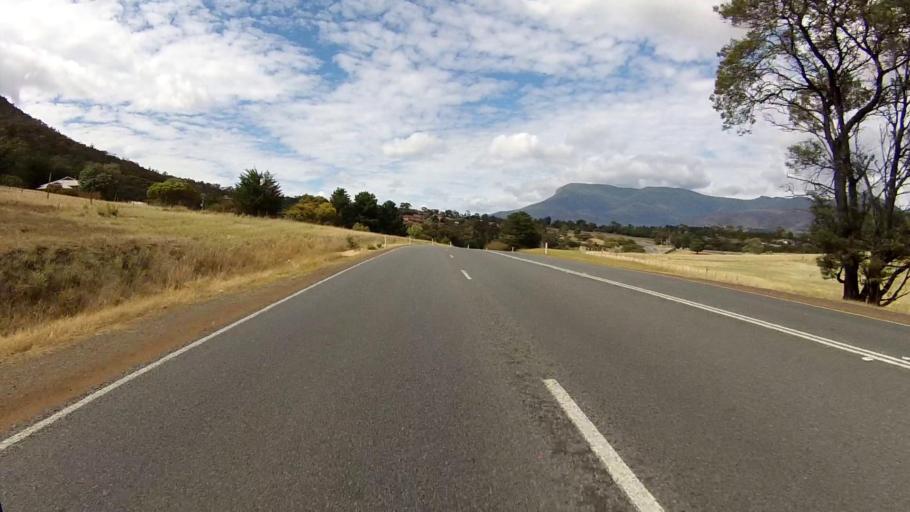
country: AU
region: Tasmania
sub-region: Brighton
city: Old Beach
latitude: -42.7926
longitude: 147.2930
